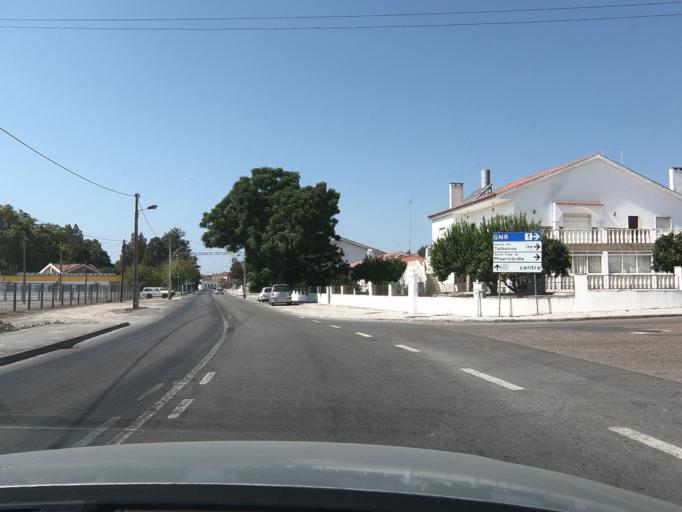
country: PT
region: Setubal
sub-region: Alcacer do Sal
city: Alcacer do Sal
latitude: 38.3698
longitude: -8.4993
